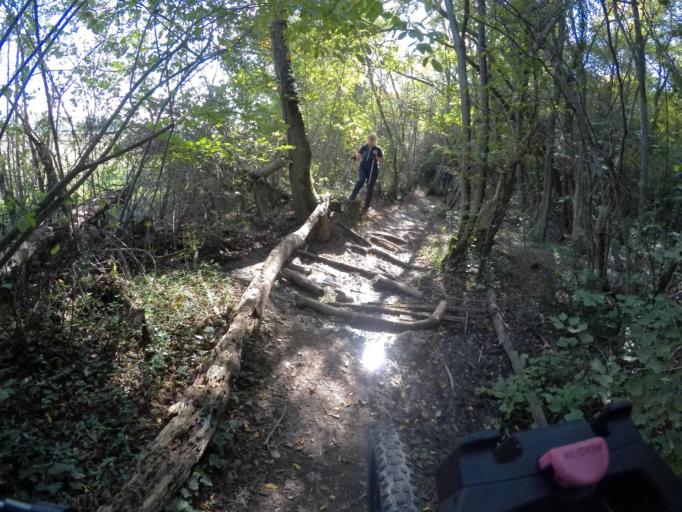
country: IT
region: Friuli Venezia Giulia
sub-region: Provincia di Udine
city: Manzano
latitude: 46.0069
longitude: 13.3810
